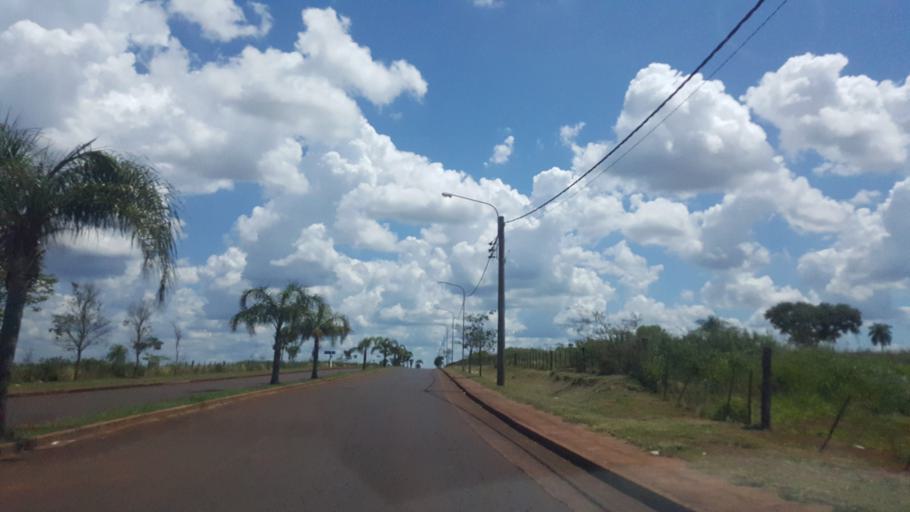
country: AR
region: Misiones
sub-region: Departamento de Capital
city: Posadas
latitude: -27.3771
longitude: -55.9616
